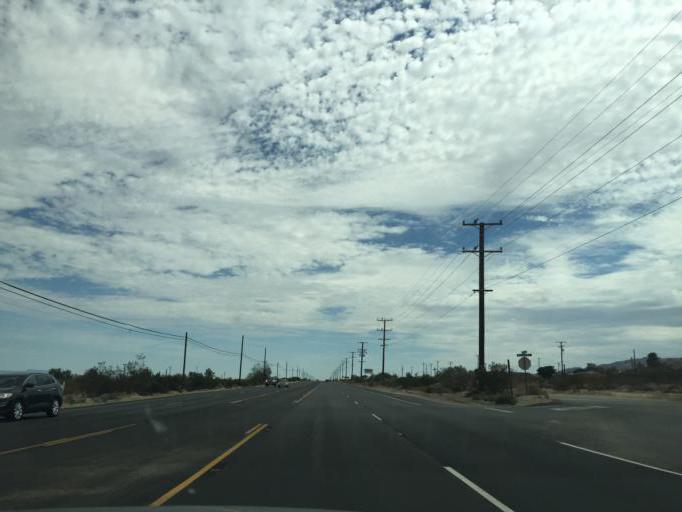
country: US
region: California
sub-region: San Bernardino County
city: Twentynine Palms
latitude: 34.1350
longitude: -116.1599
